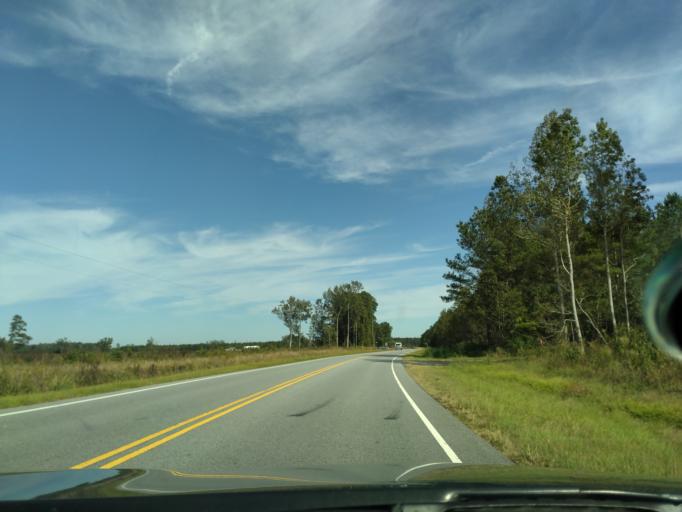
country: US
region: North Carolina
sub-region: Beaufort County
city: River Road
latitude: 35.5242
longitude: -76.8868
